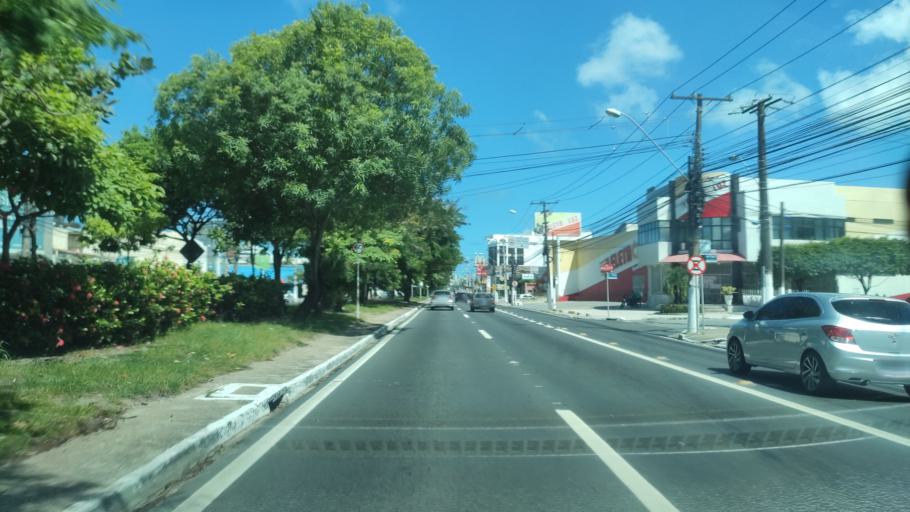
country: BR
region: Alagoas
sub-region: Maceio
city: Maceio
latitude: -9.6421
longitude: -35.7351
